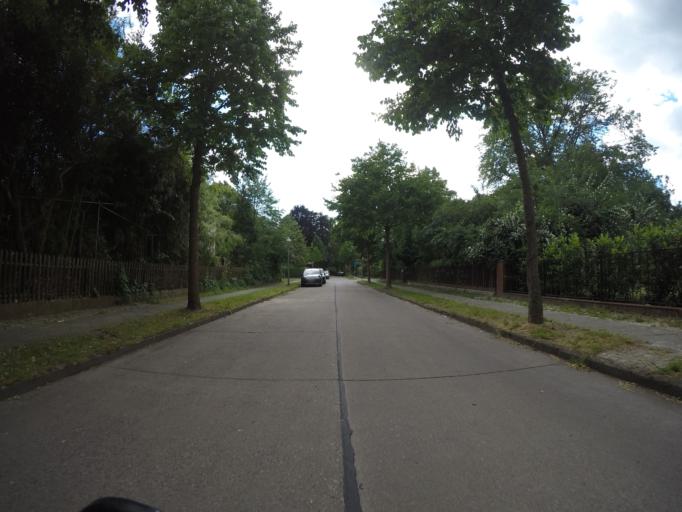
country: DE
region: Berlin
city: Zehlendorf Bezirk
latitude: 52.4250
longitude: 13.2673
